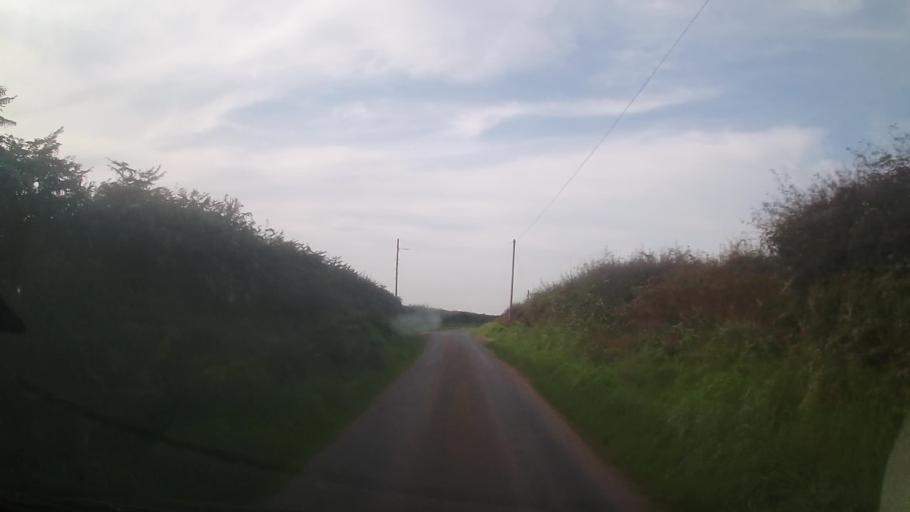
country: GB
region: Wales
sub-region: Pembrokeshire
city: Camrose
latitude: 51.8822
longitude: -5.0505
